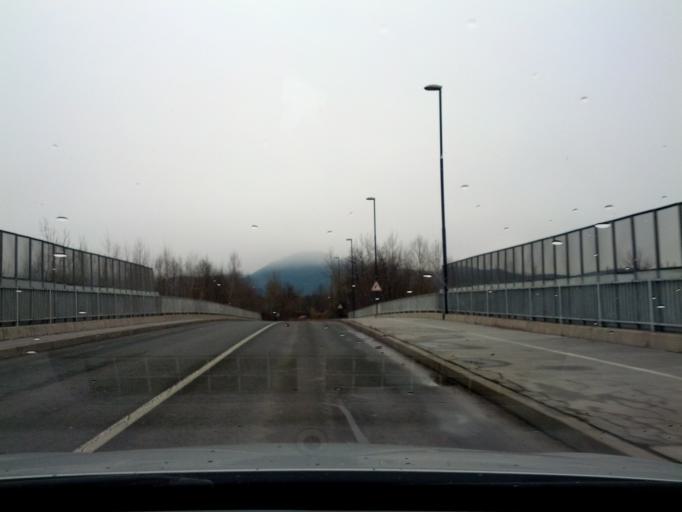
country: SI
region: Ljubljana
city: Ljubljana
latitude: 46.0259
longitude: 14.4990
